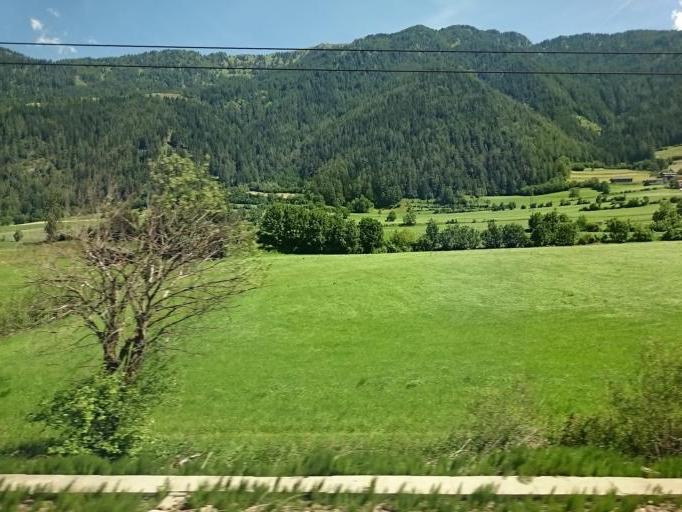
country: IT
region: Trentino-Alto Adige
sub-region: Bolzano
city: Campo di Trens
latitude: 46.8657
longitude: 11.4958
